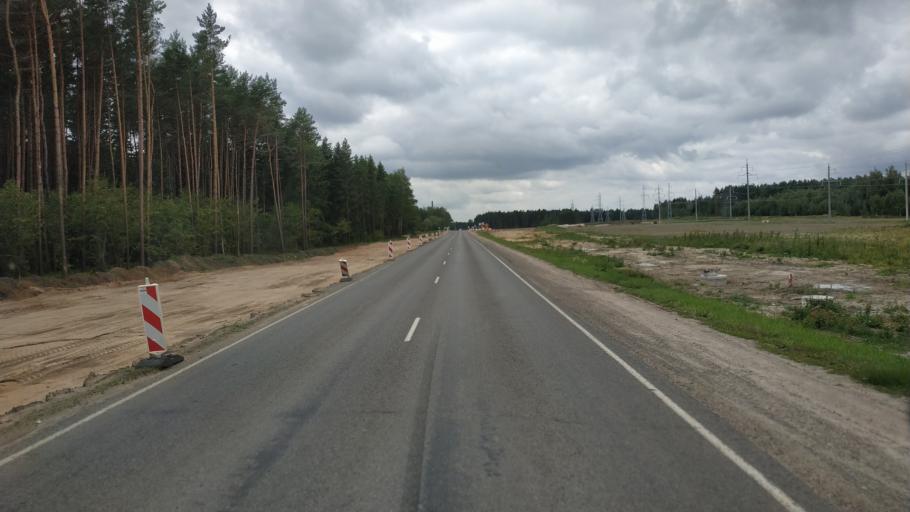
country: BY
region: Mogilev
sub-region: Mahilyowski Rayon
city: Veyno
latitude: 53.8742
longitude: 30.4383
